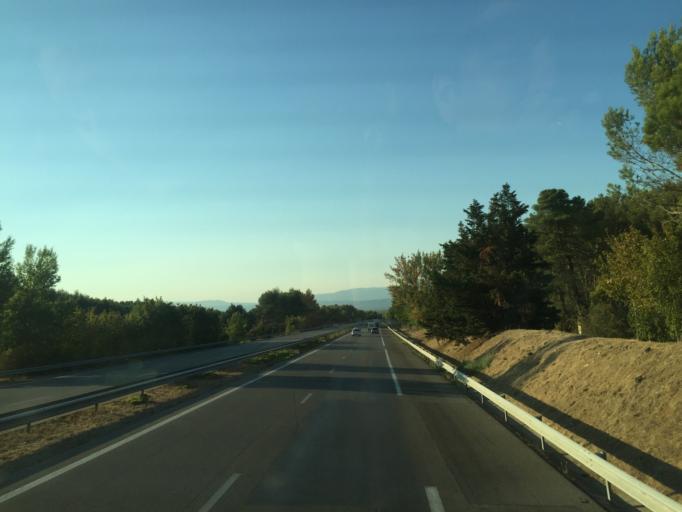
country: FR
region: Provence-Alpes-Cote d'Azur
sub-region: Departement des Bouches-du-Rhone
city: Venelles
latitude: 43.6162
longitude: 5.4959
